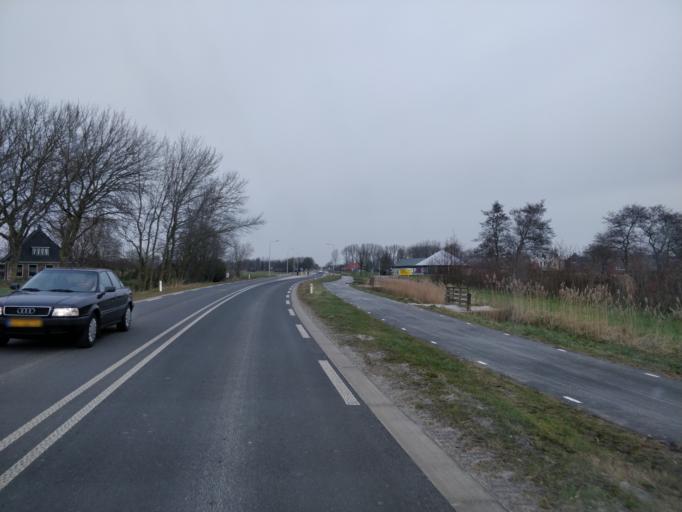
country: NL
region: Friesland
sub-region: Gemeente Ferwerderadiel
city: Marrum
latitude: 53.3214
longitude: 5.7957
